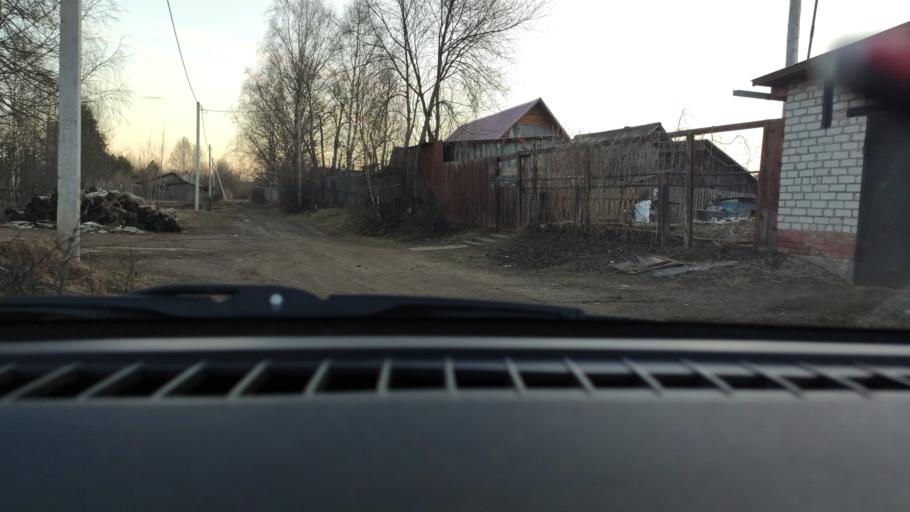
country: RU
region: Perm
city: Perm
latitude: 58.0818
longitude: 56.3188
